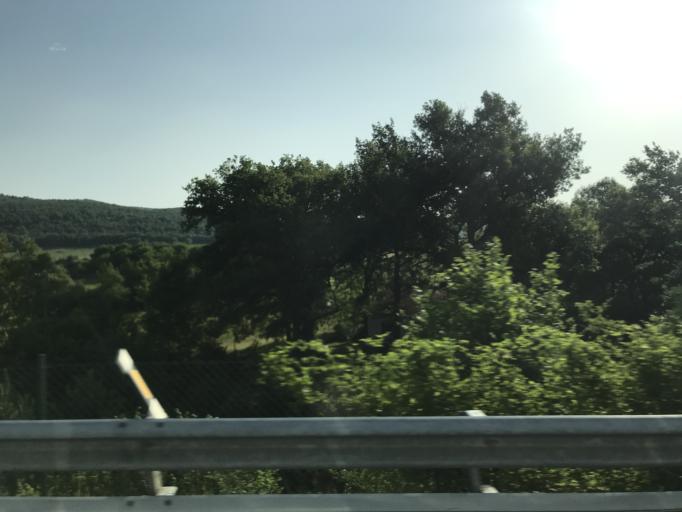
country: ES
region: Navarre
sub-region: Provincia de Navarra
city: Altsasu
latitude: 42.9118
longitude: -2.1787
